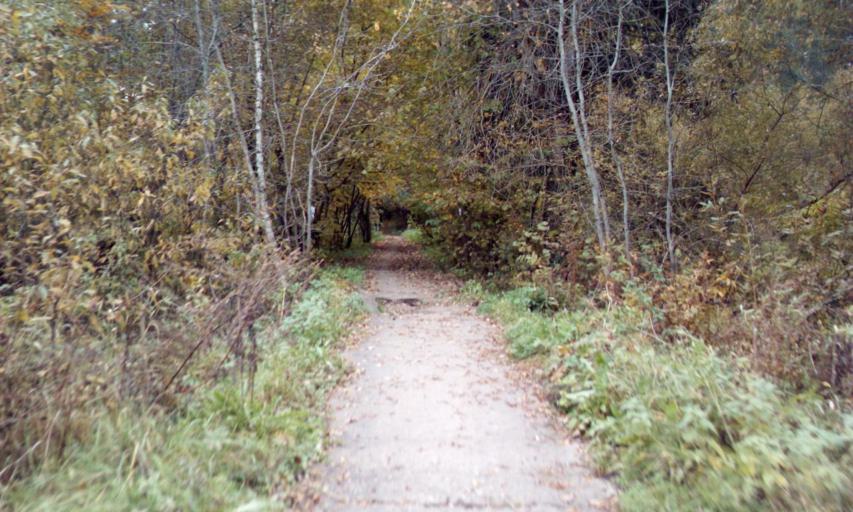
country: RU
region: Moskovskaya
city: Lesnoy Gorodok
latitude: 55.6866
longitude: 37.2134
